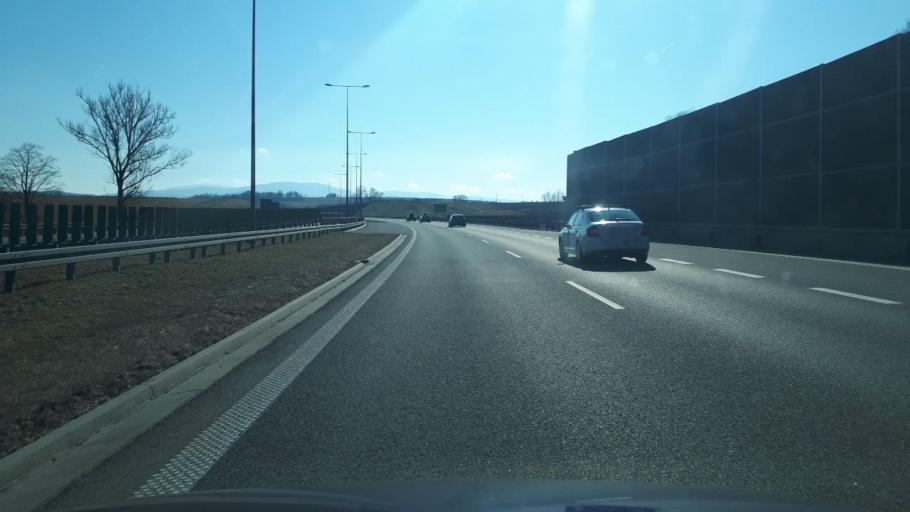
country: PL
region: Silesian Voivodeship
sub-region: Powiat zywiecki
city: Lodygowice
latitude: 49.7070
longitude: 19.1208
